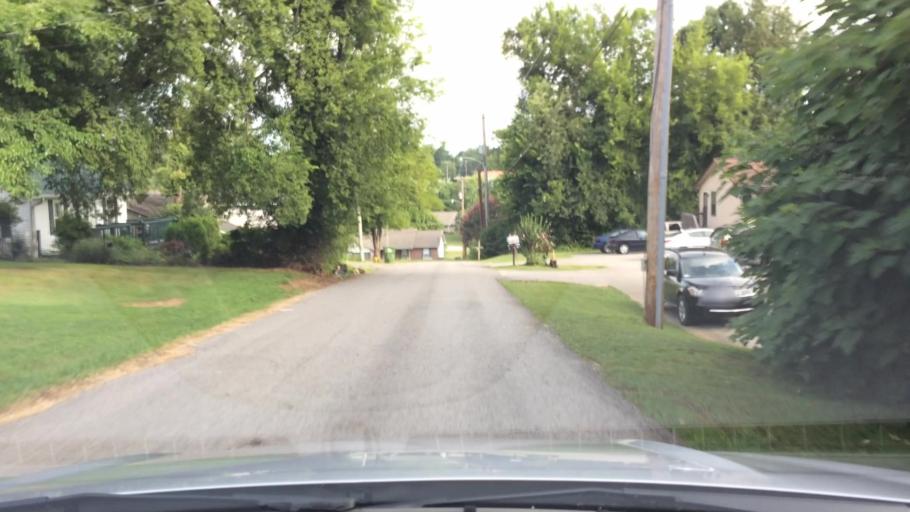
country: US
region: Tennessee
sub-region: Blount County
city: Eagleton Village
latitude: 35.7631
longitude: -83.9333
